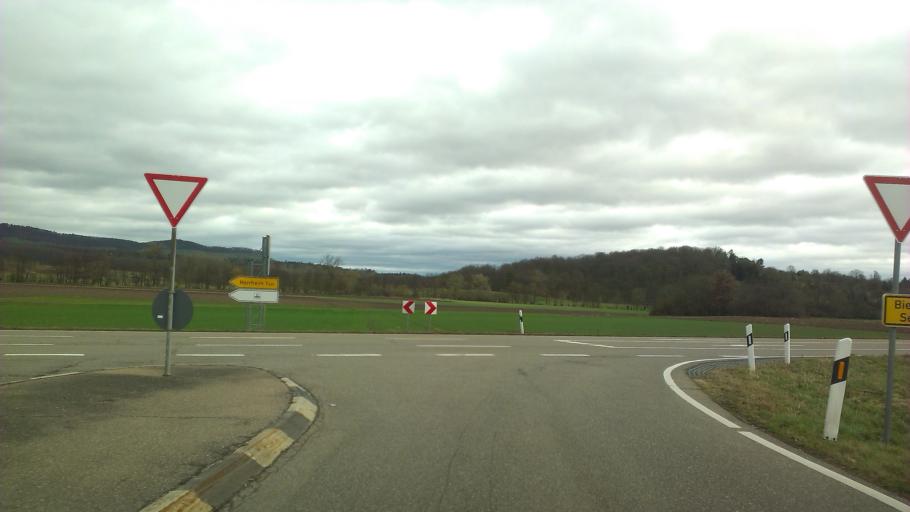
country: DE
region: Baden-Wuerttemberg
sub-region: Regierungsbezirk Stuttgart
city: Sersheim
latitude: 48.9726
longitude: 8.9925
